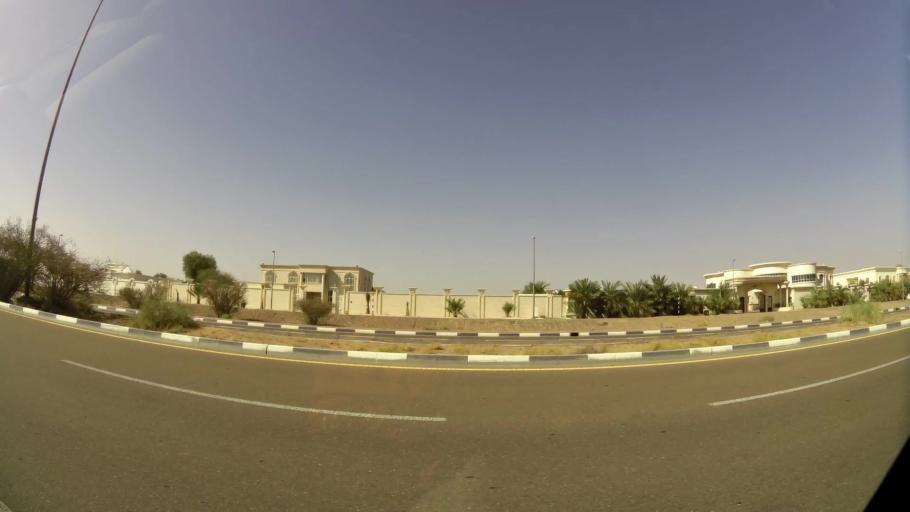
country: OM
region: Al Buraimi
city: Al Buraymi
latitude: 24.3418
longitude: 55.7975
